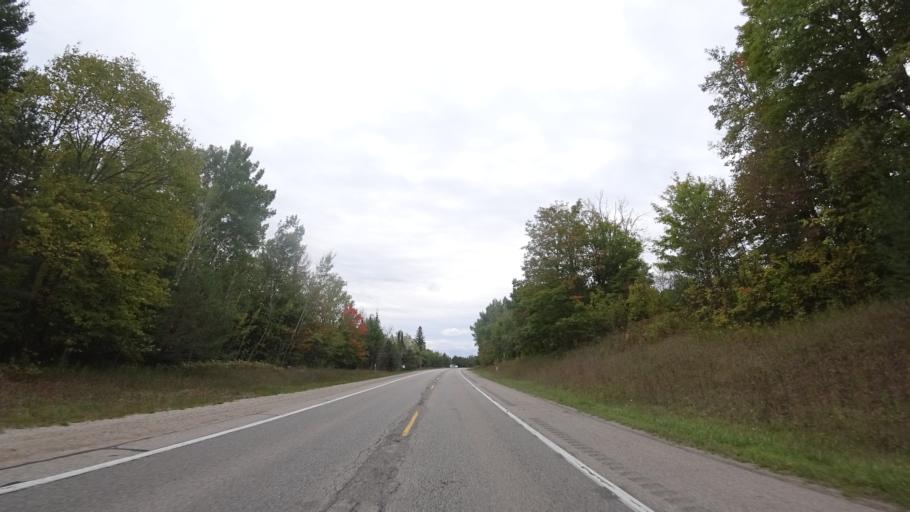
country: US
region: Michigan
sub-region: Charlevoix County
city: Boyne City
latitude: 45.2384
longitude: -84.9165
